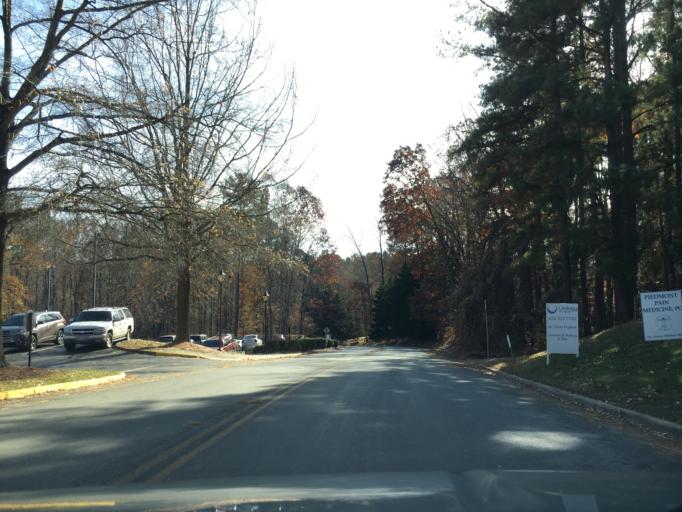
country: US
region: Virginia
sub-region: Halifax County
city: South Boston
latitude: 36.7114
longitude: -78.9146
